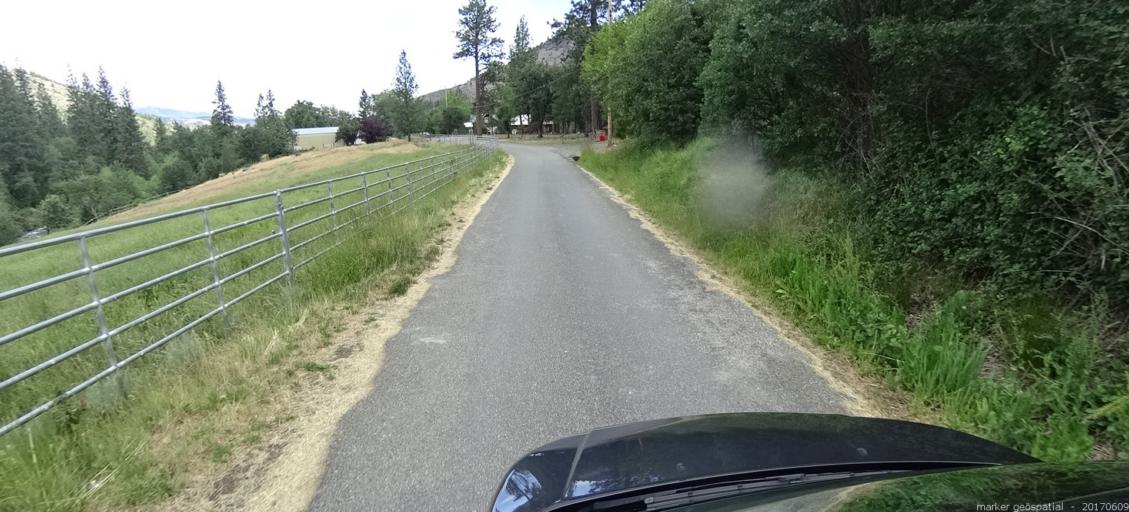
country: US
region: California
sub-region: Siskiyou County
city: Weed
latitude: 41.3048
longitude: -122.7986
